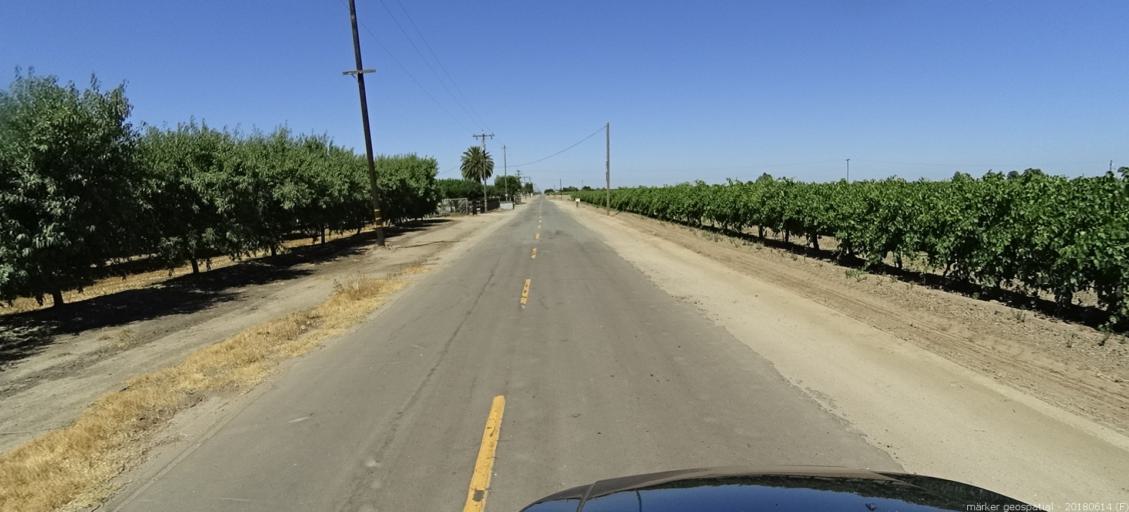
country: US
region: California
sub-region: Madera County
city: Fairmead
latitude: 36.9892
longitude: -120.2095
